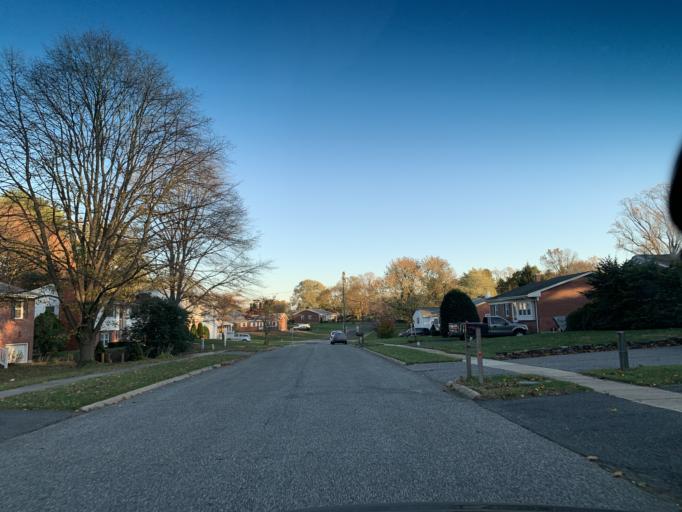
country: US
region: Maryland
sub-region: Harford County
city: Bel Air North
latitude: 39.5588
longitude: -76.3764
